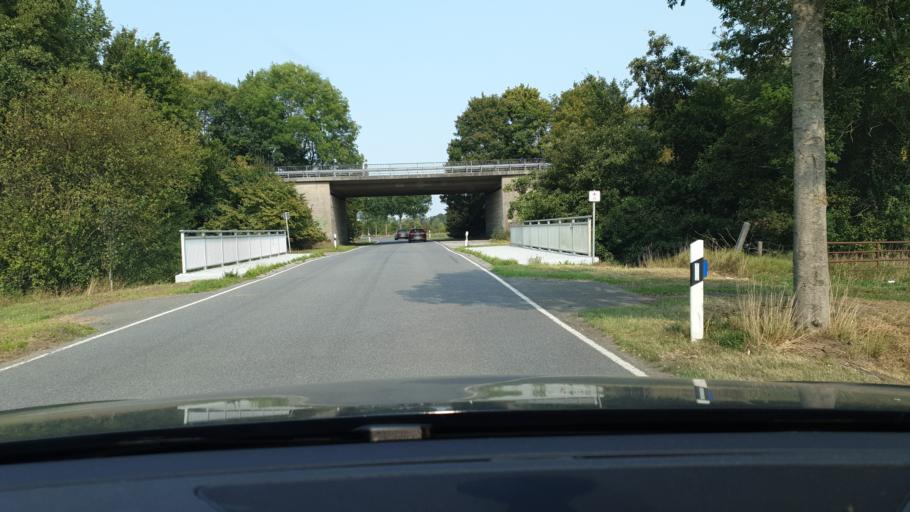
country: DE
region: North Rhine-Westphalia
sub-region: Regierungsbezirk Dusseldorf
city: Kranenburg
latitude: 51.7999
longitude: 6.0149
